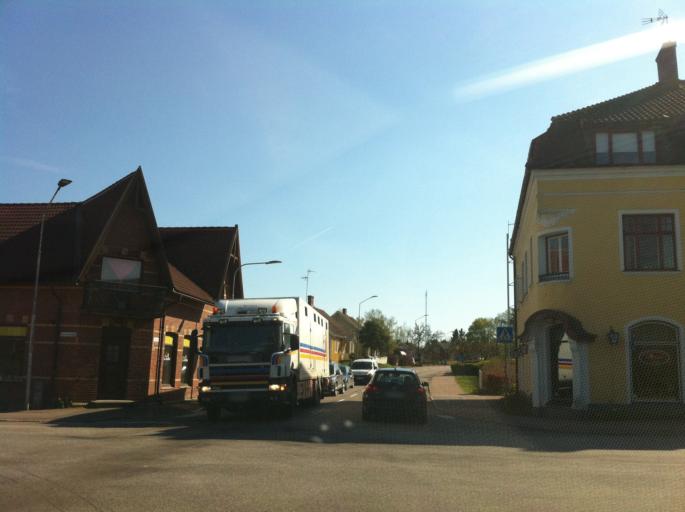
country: SE
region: Skane
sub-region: Svalovs Kommun
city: Kagerod
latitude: 56.0358
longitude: 13.0997
